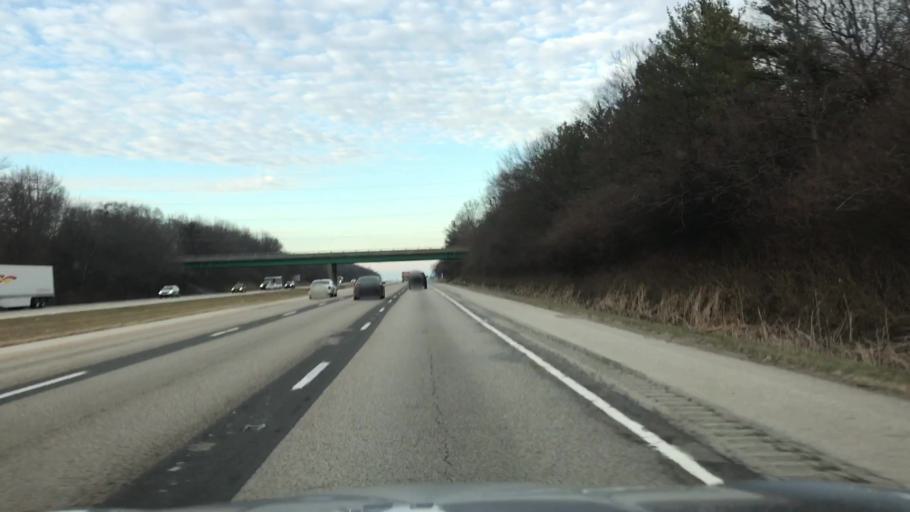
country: US
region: Illinois
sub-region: Logan County
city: Lincoln
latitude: 40.1454
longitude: -89.4171
